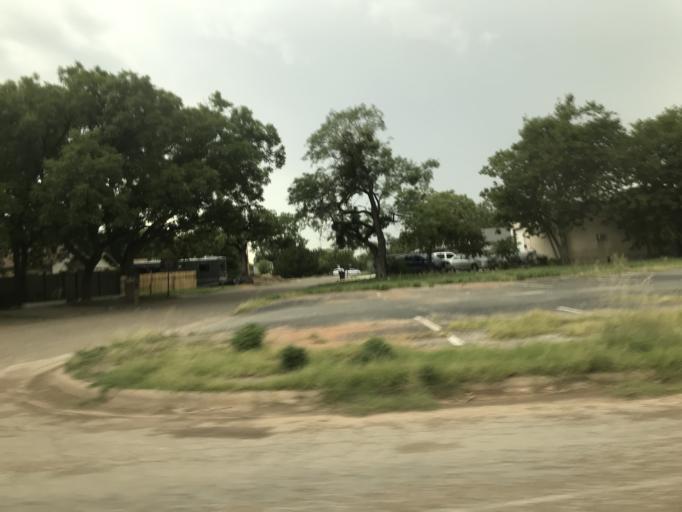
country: US
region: Texas
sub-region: Taylor County
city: Abilene
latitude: 32.4493
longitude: -99.7565
